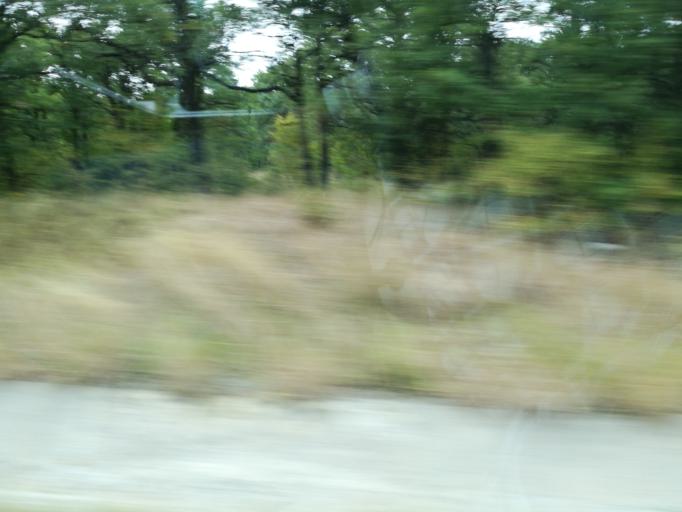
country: RO
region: Tulcea
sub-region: Comuna Horia
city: Horia
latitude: 44.9963
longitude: 28.4503
